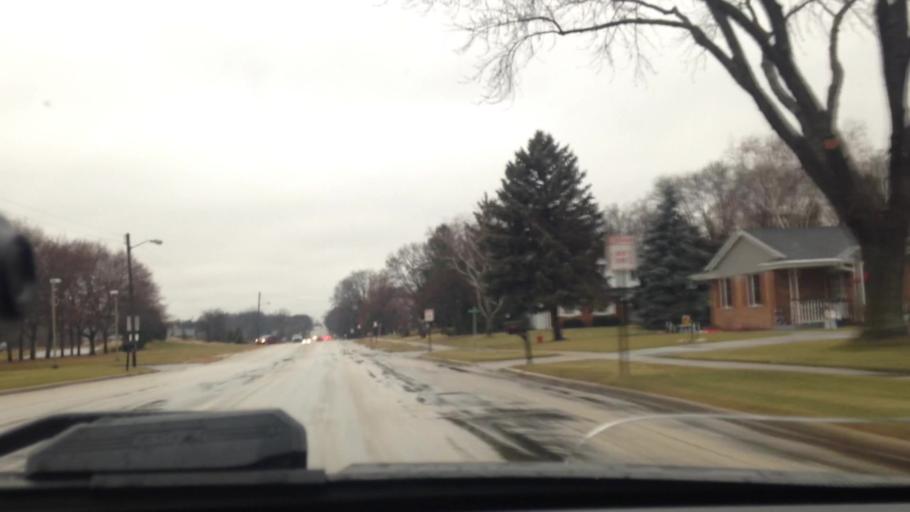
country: US
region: Wisconsin
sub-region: Waukesha County
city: Menomonee Falls
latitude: 43.1703
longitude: -88.1263
